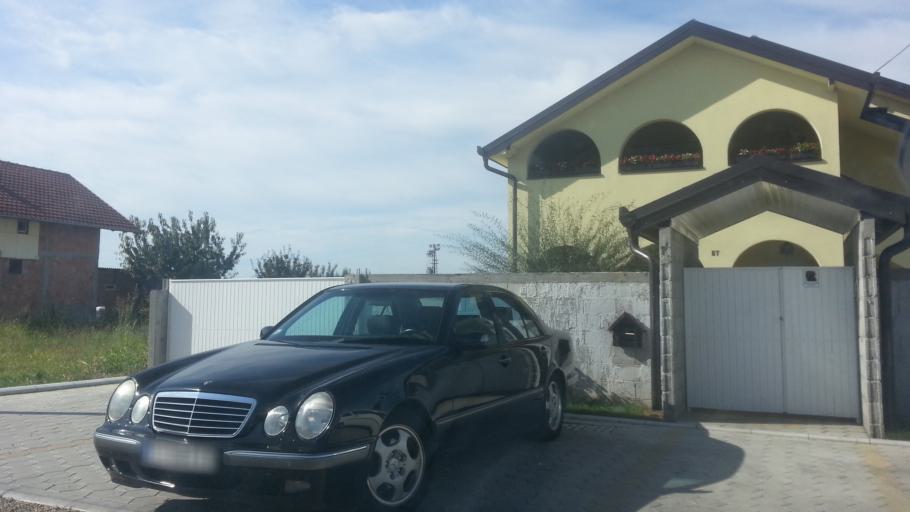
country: RS
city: Novi Banovci
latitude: 44.9704
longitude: 20.2713
